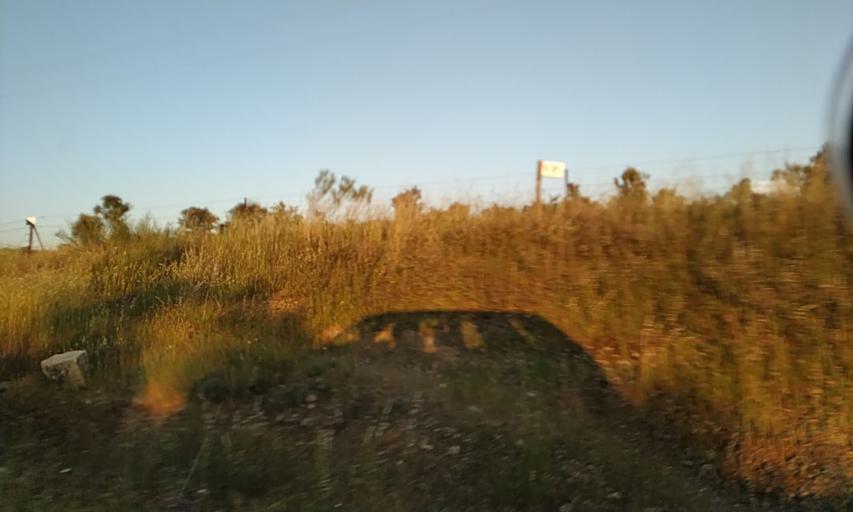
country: ES
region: Extremadura
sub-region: Provincia de Caceres
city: Salorino
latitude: 39.5377
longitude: -7.0351
